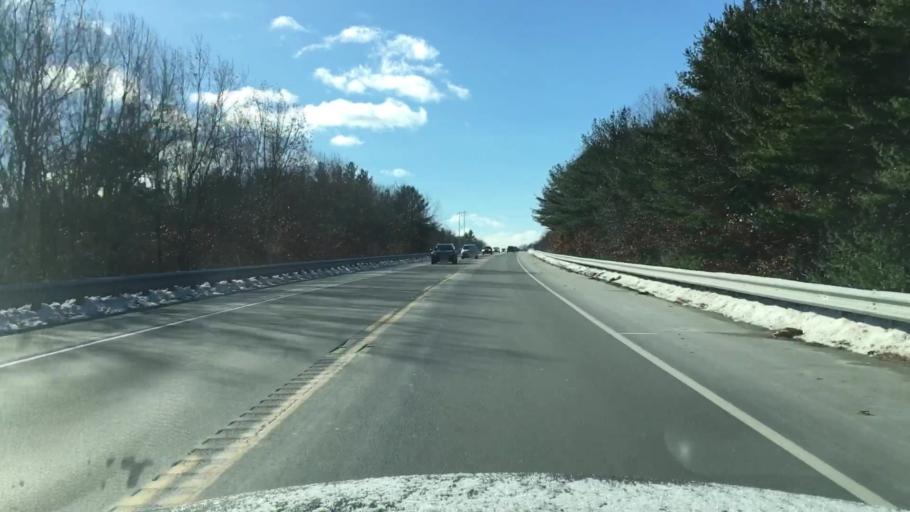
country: US
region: New Hampshire
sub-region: Hillsborough County
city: Milford
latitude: 42.8468
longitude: -71.6144
